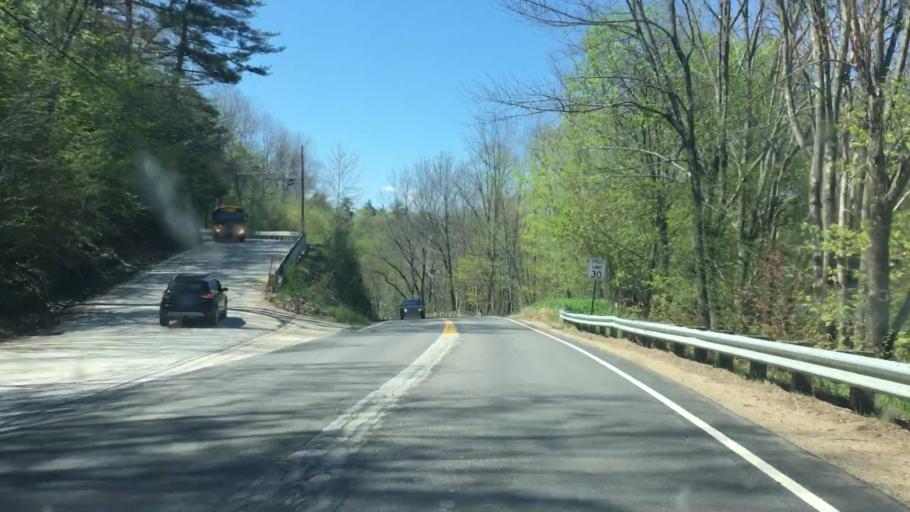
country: US
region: New Hampshire
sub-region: Grafton County
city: Plymouth
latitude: 43.7489
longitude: -71.6845
